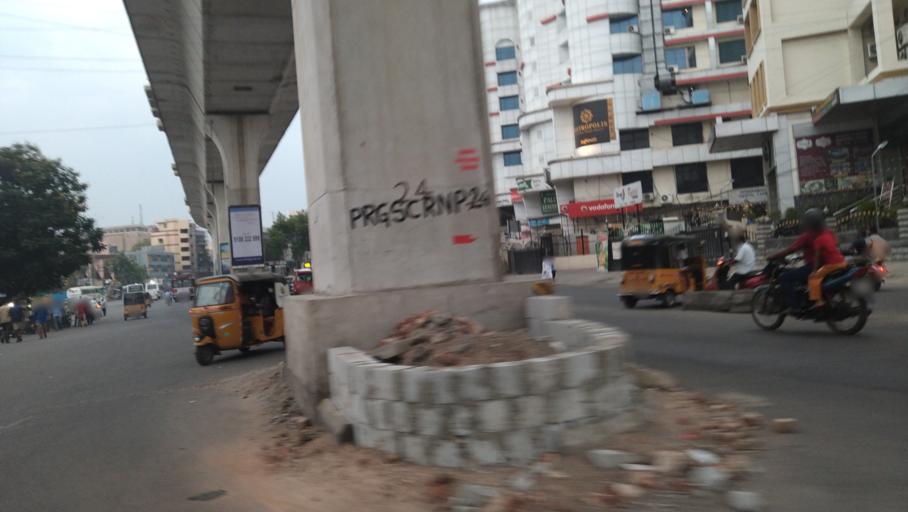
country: IN
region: Telangana
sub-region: Hyderabad
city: Malkajgiri
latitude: 17.4381
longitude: 78.4994
